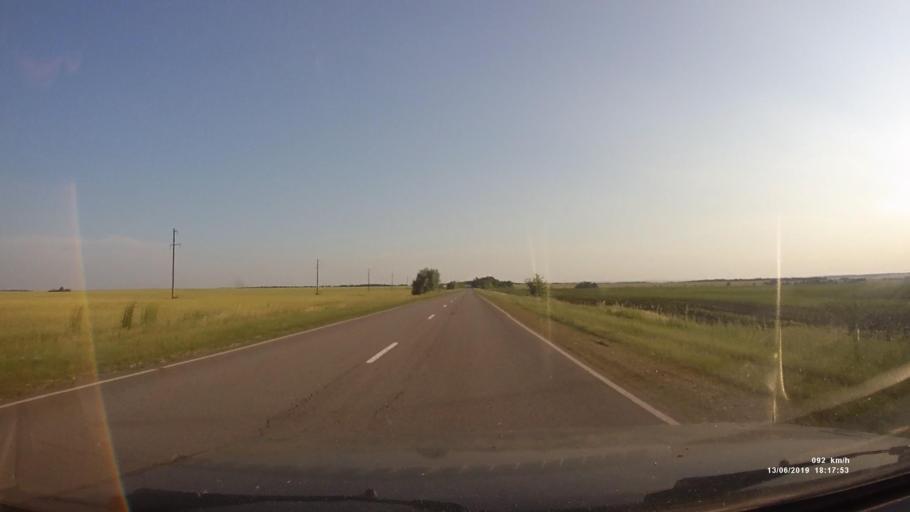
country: RU
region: Rostov
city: Kazanskaya
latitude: 49.9146
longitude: 41.3201
